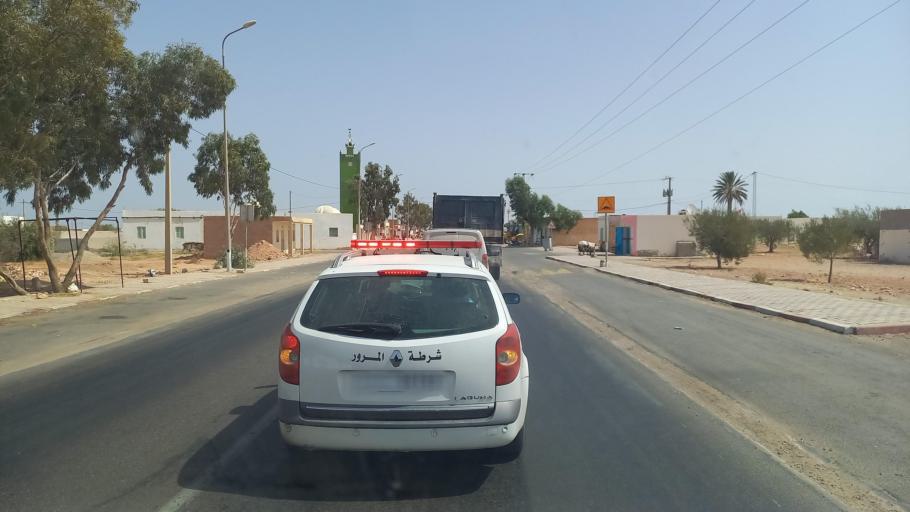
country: TN
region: Madanin
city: Medenine
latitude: 33.3728
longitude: 10.6920
